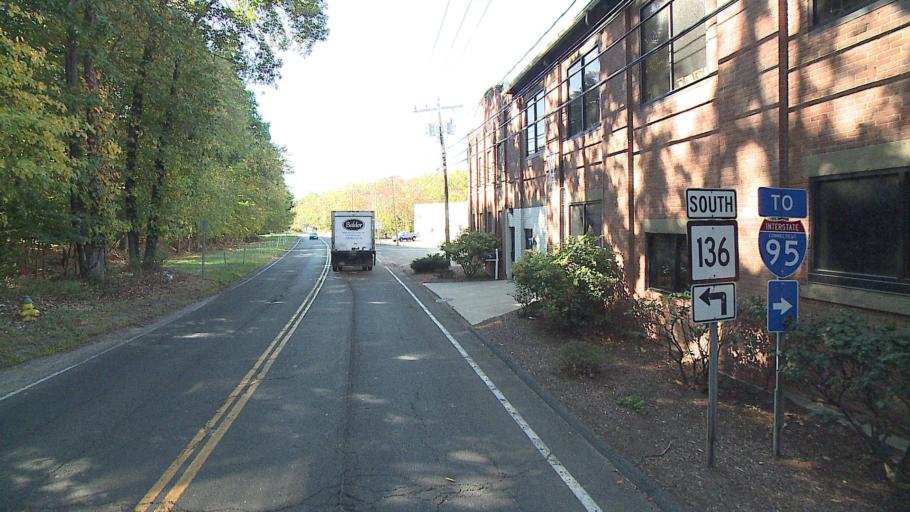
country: US
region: Connecticut
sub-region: Fairfield County
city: East Norwalk
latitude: 41.0770
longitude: -73.4265
